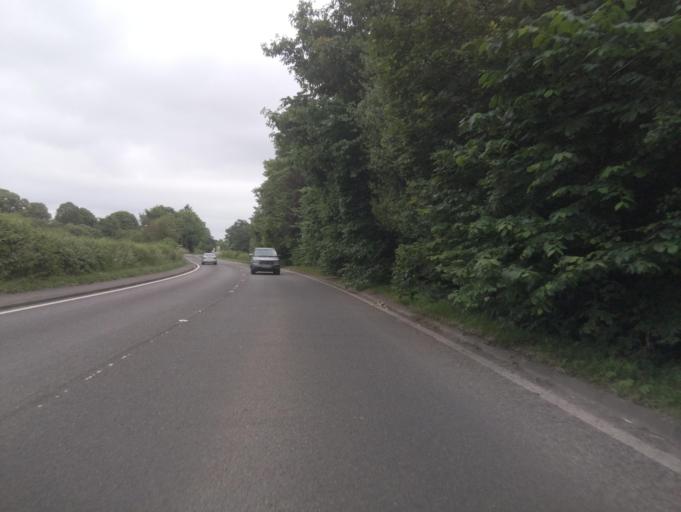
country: GB
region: England
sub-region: Derbyshire
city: Findern
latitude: 52.9405
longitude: -1.5515
